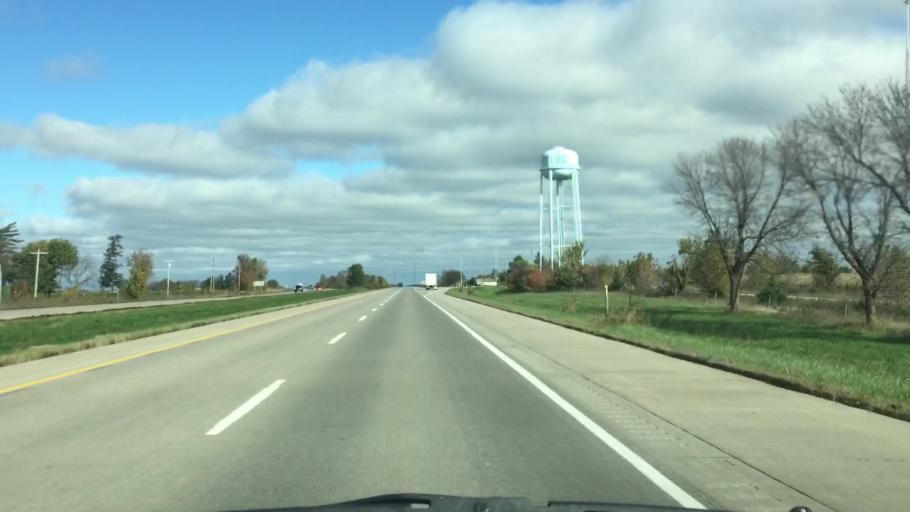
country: US
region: Iowa
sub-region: Clarke County
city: Osceola
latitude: 40.9841
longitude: -93.7975
